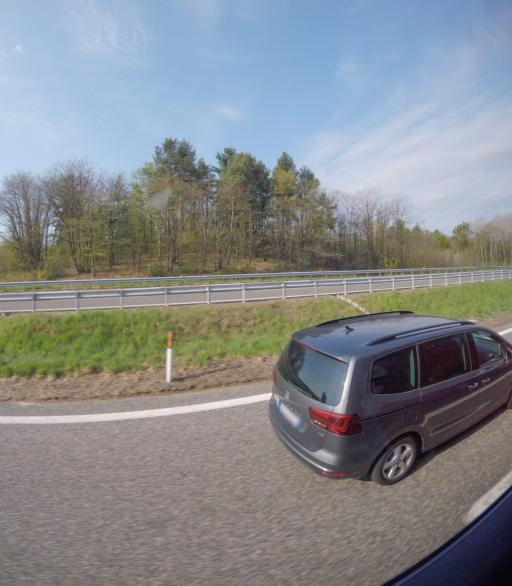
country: IT
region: Piedmont
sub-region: Provincia di Novara
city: Comignago
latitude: 45.7088
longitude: 8.5462
